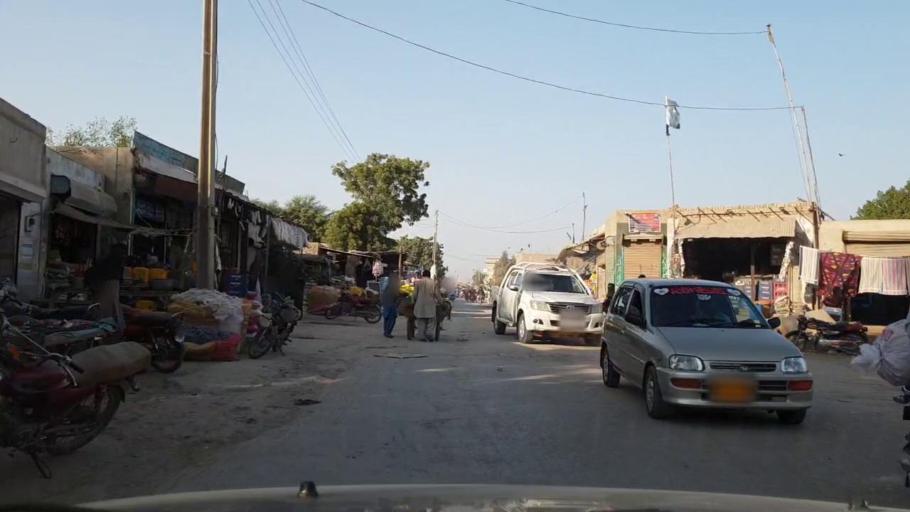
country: PK
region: Sindh
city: Chambar
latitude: 25.2142
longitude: 68.7796
